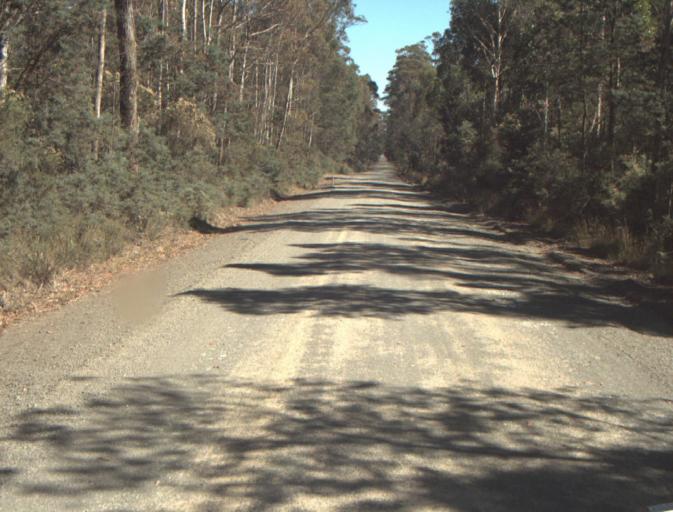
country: AU
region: Tasmania
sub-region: Launceston
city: Newstead
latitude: -41.3644
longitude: 147.2317
